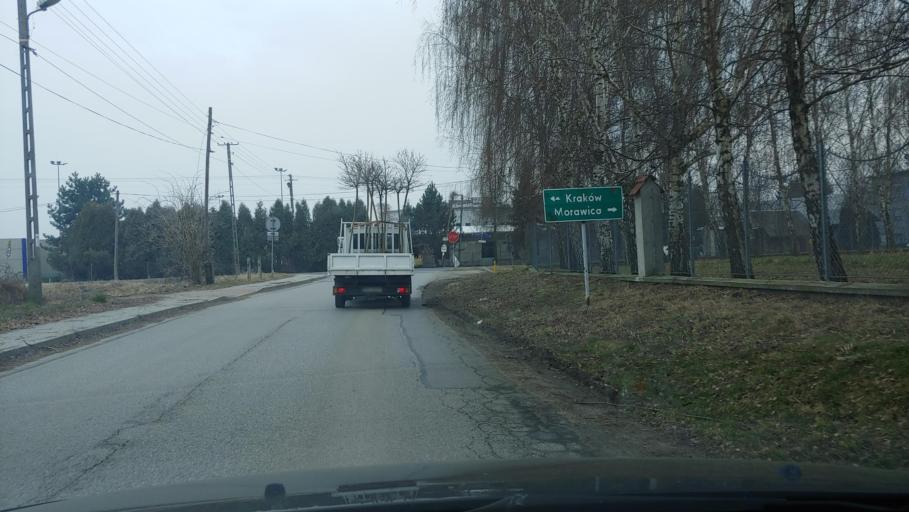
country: PL
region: Lesser Poland Voivodeship
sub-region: Powiat krakowski
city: Balice
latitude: 50.0844
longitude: 19.7896
